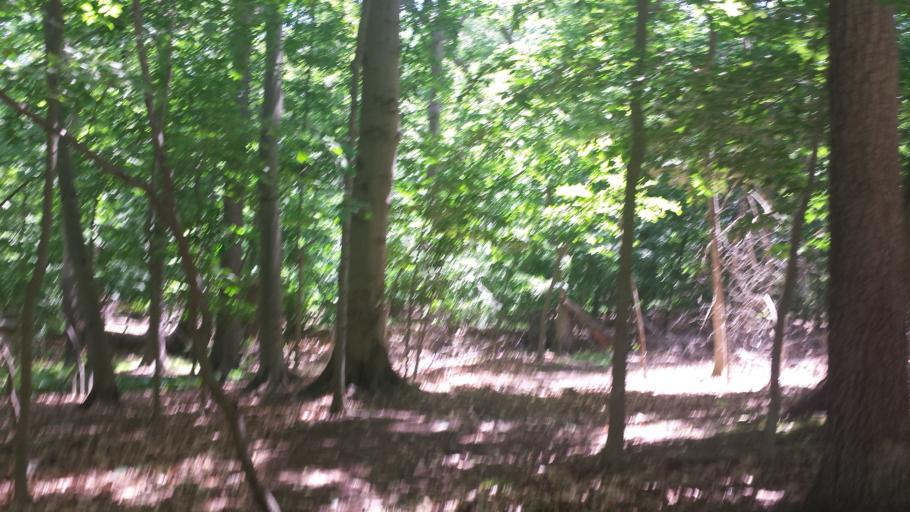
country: US
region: New York
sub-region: Westchester County
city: Harrison
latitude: 40.9539
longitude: -73.7014
